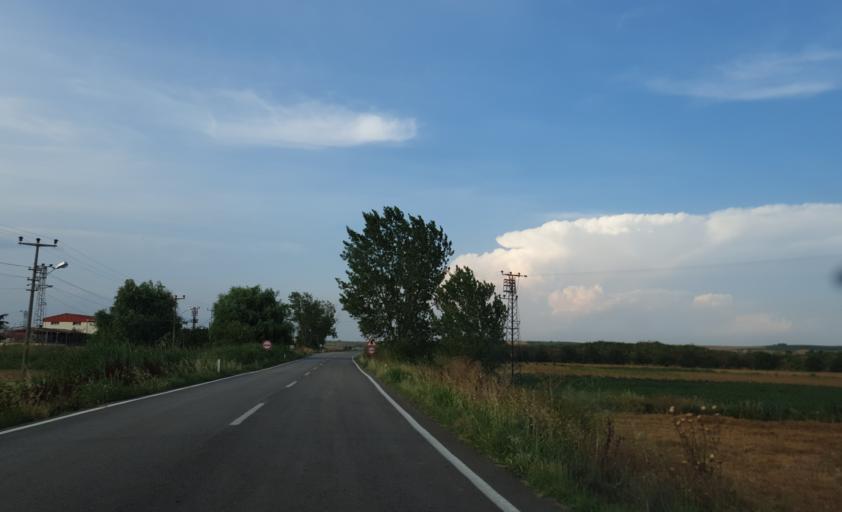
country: TR
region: Tekirdag
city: Hayrabolu
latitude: 41.2304
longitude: 27.1223
